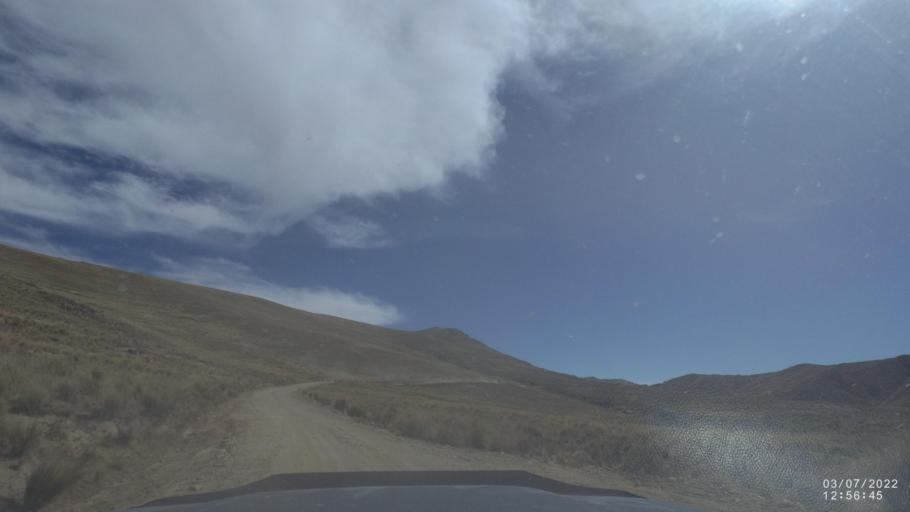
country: BO
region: Cochabamba
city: Sipe Sipe
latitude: -17.7275
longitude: -66.6730
